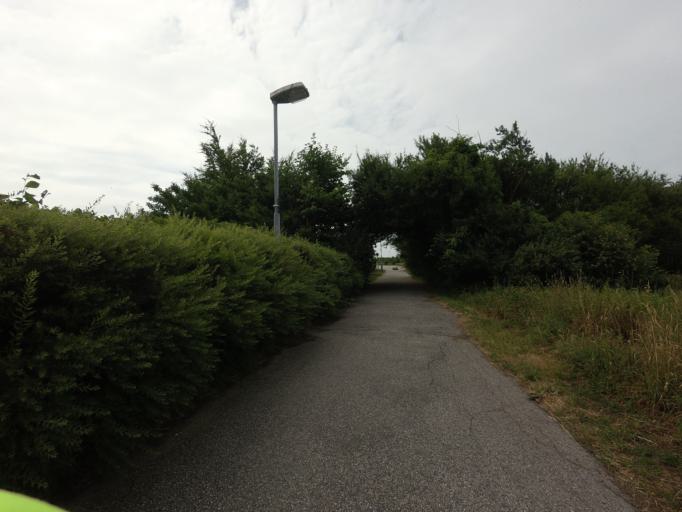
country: SE
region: Skane
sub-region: Malmo
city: Bunkeflostrand
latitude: 55.5599
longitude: 12.9081
